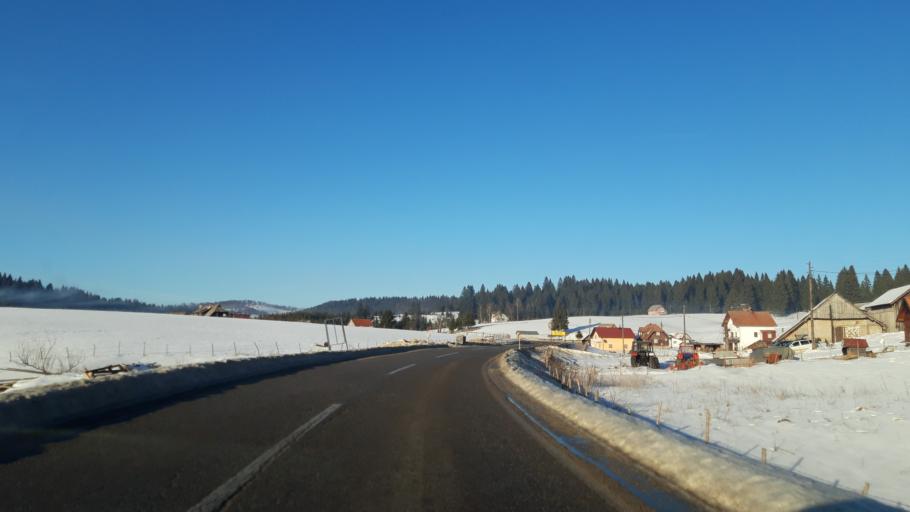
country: BA
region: Republika Srpska
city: Han Pijesak
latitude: 44.1051
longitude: 18.9700
